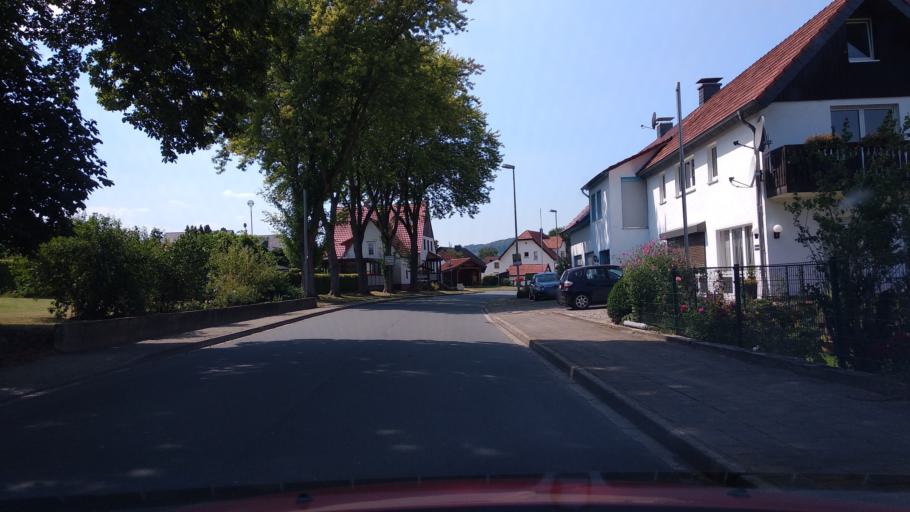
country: DE
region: North Rhine-Westphalia
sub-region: Regierungsbezirk Detmold
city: Bad Driburg
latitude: 51.7105
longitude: 9.0968
